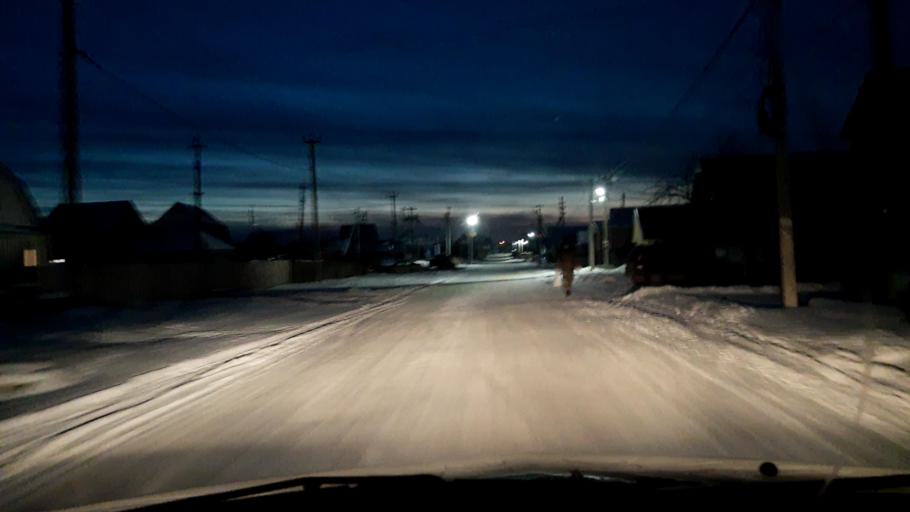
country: RU
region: Bashkortostan
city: Ufa
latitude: 54.6154
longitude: 55.9473
